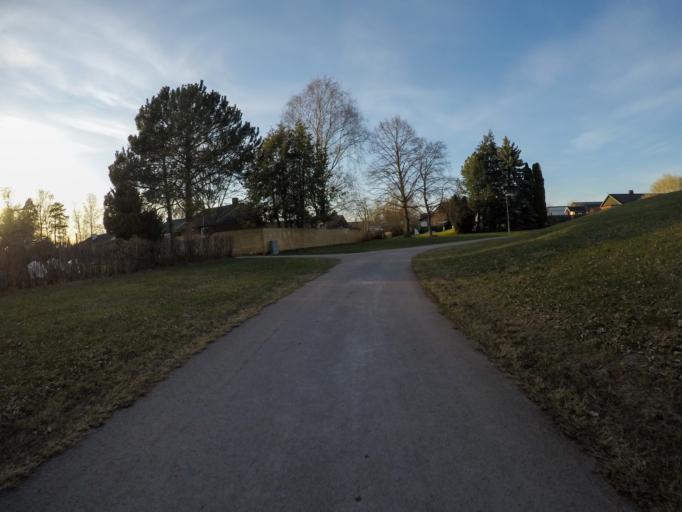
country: SE
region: Vaestmanland
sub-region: Vasteras
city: Vasteras
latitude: 59.5982
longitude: 16.6097
